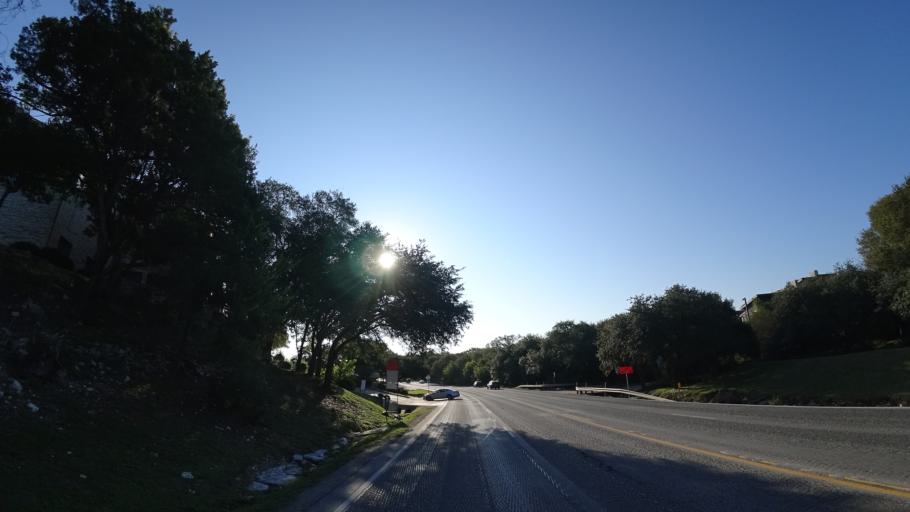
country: US
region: Texas
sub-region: Travis County
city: Rollingwood
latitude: 30.2713
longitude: -97.7941
